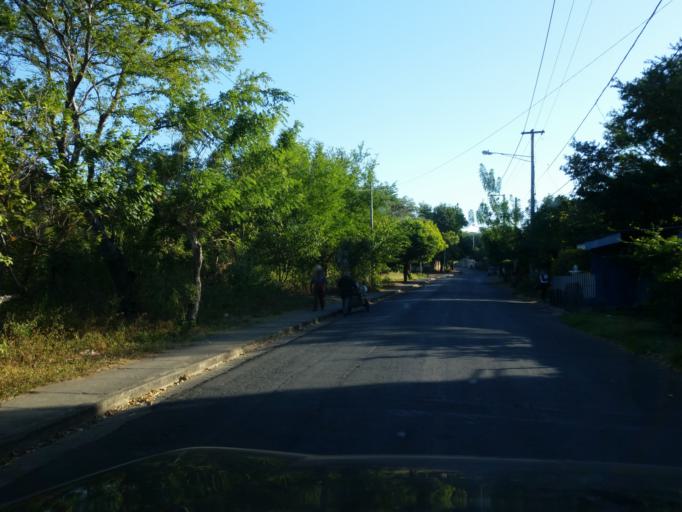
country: NI
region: Managua
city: Managua
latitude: 12.1244
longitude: -86.2886
